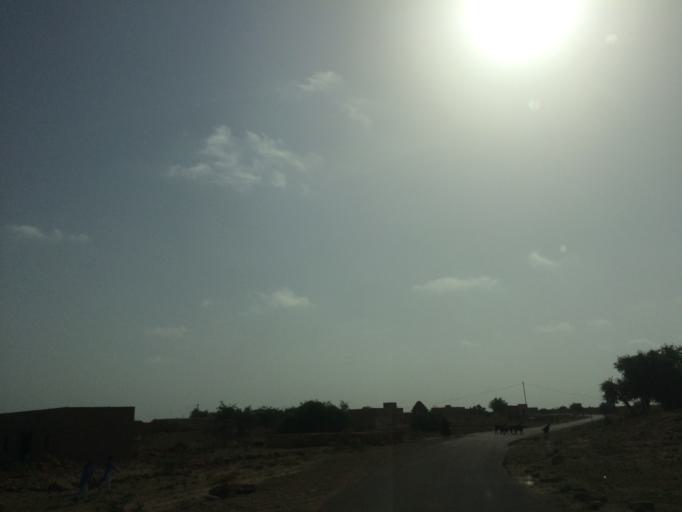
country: IN
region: Rajasthan
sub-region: Jaisalmer
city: Jaisalmer
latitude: 26.8214
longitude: 70.7119
